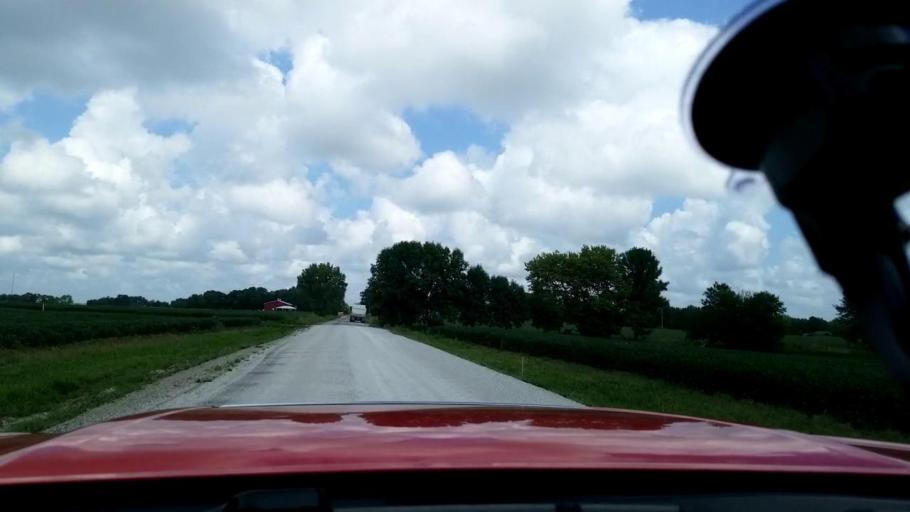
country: US
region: Iowa
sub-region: Decatur County
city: Lamoni
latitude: 40.7026
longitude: -94.0531
